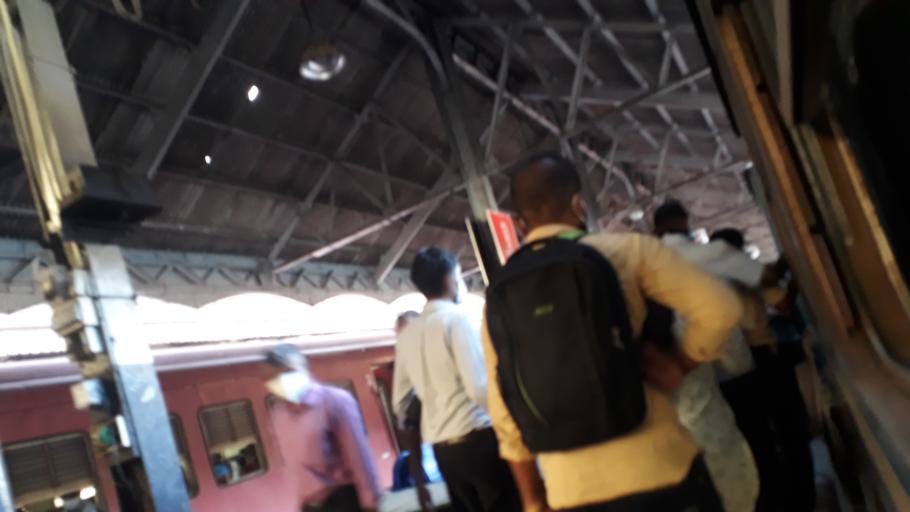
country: LK
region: Western
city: Colombo
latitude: 6.9335
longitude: 79.8504
